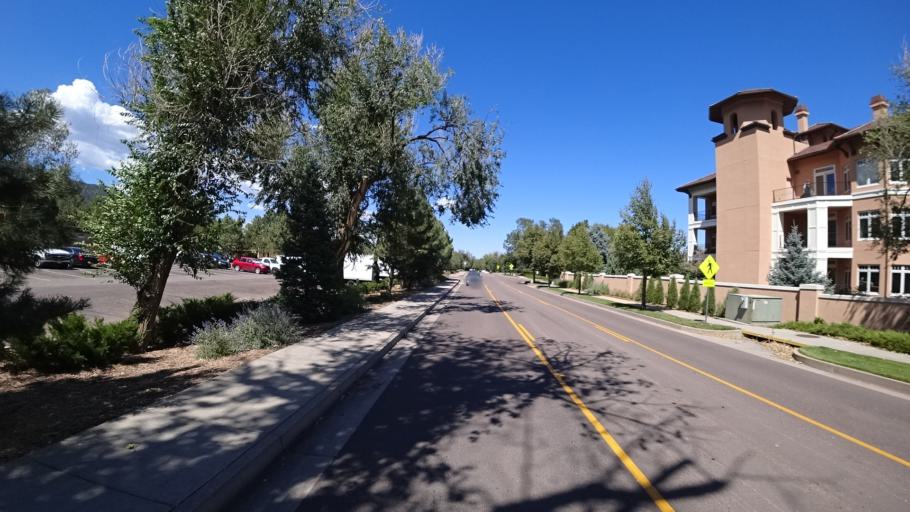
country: US
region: Colorado
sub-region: El Paso County
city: Colorado Springs
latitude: 38.7887
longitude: -104.8548
